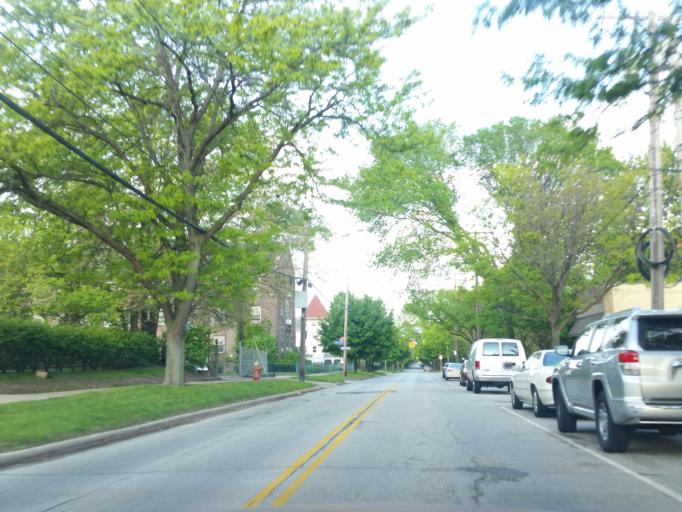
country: US
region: Ohio
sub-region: Cuyahoga County
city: Cleveland
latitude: 41.4871
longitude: -81.7104
